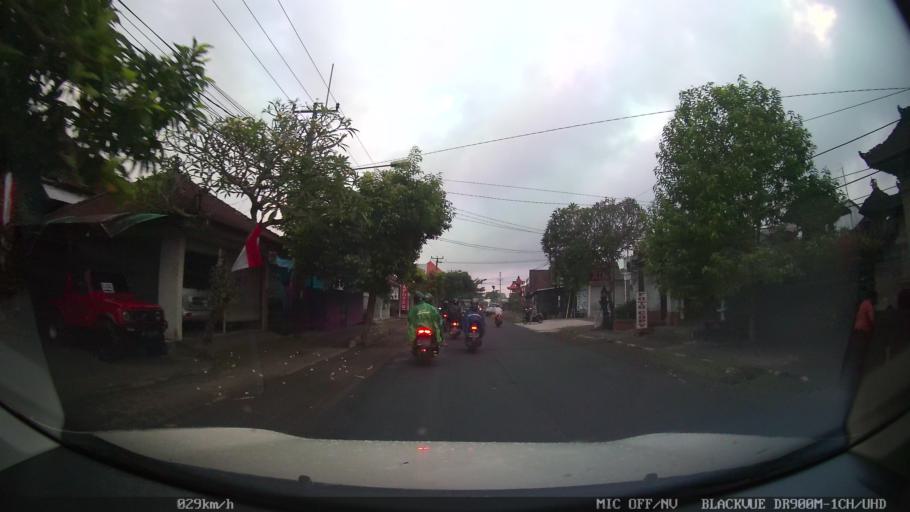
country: ID
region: Bali
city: Banjar Parekan
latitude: -8.5637
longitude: 115.2207
